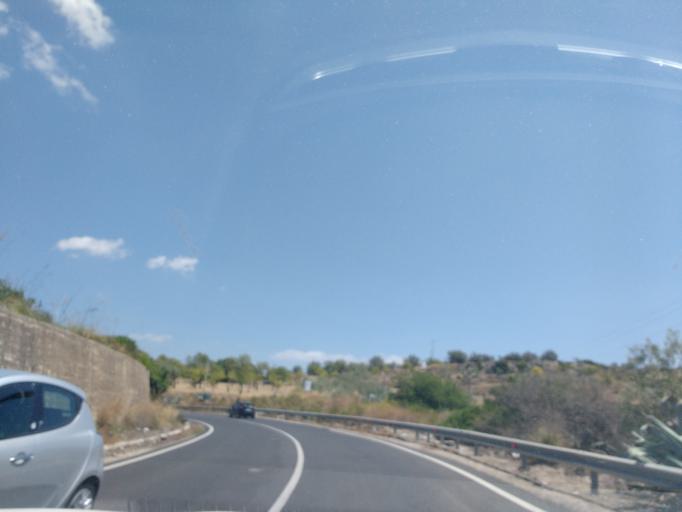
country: IT
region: Sicily
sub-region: Provincia di Siracusa
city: Noto
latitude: 36.8685
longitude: 15.0353
